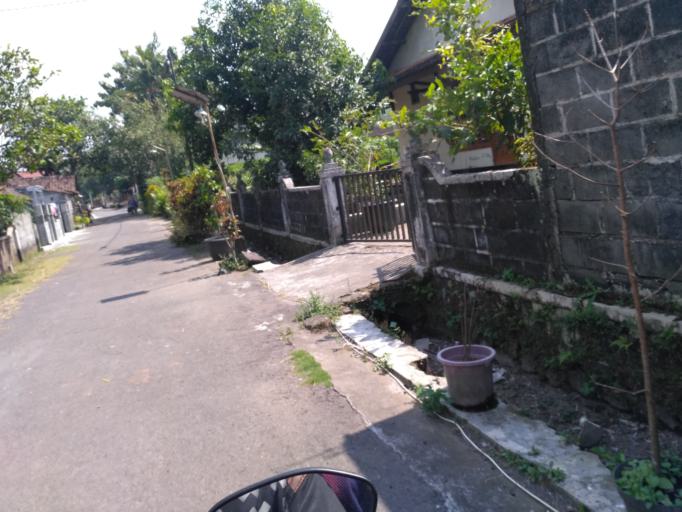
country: ID
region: Daerah Istimewa Yogyakarta
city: Depok
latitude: -7.7078
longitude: 110.4182
